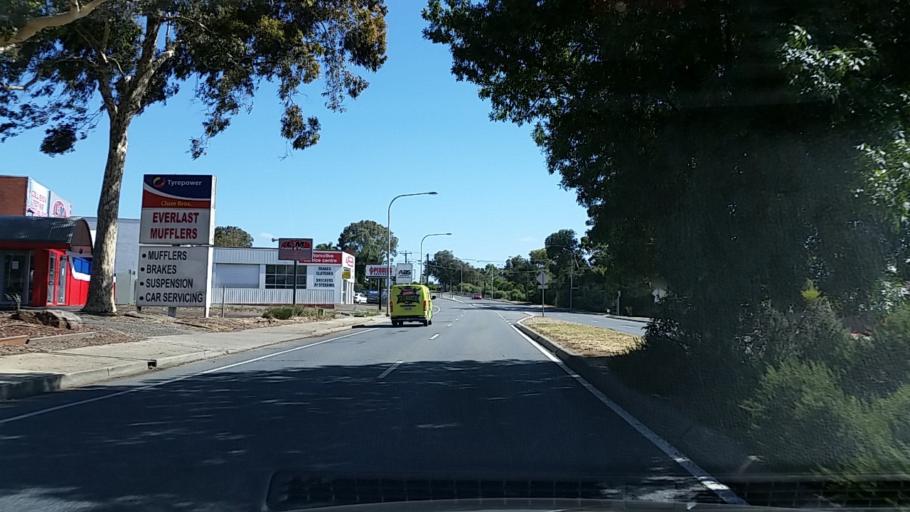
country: AU
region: South Australia
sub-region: Tea Tree Gully
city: Hope Valley
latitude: -34.8242
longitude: 138.6941
